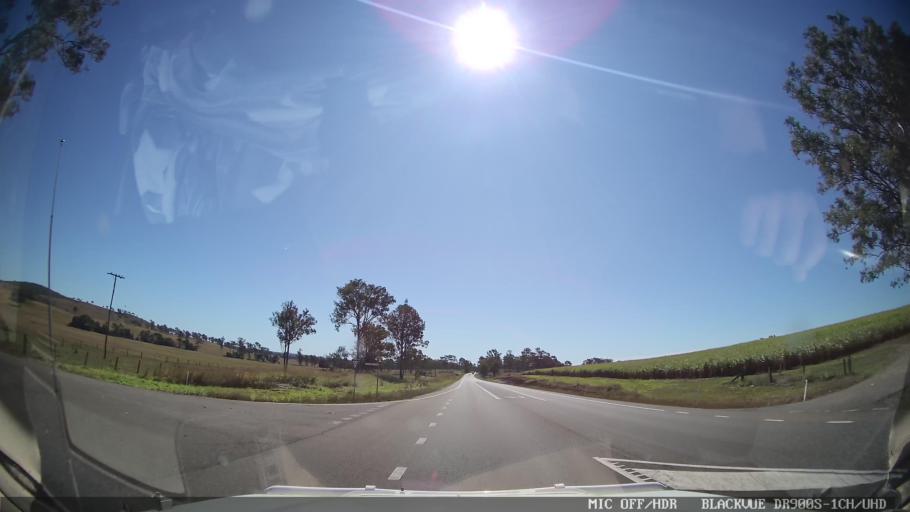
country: AU
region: Queensland
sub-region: Fraser Coast
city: Maryborough
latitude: -25.7792
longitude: 152.5964
